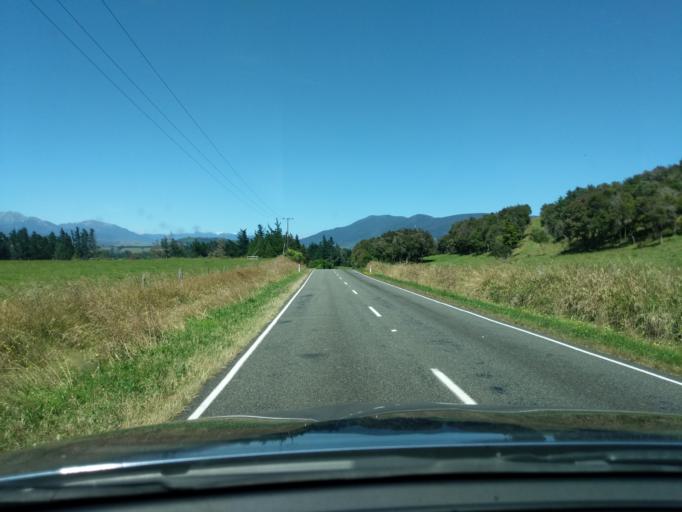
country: NZ
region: Tasman
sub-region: Tasman District
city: Takaka
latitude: -40.6922
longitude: 172.6423
